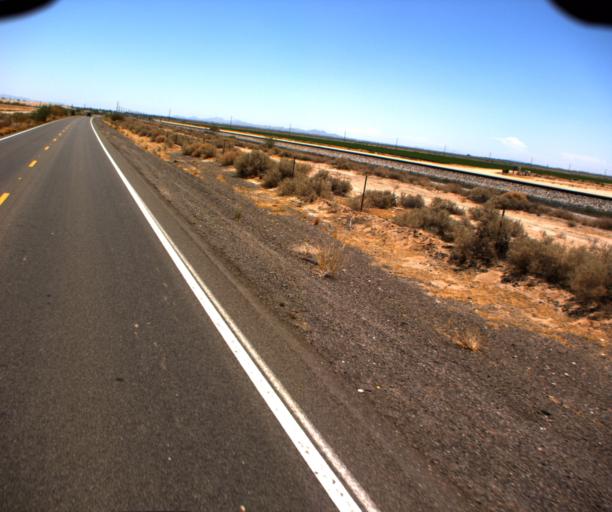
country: US
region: Arizona
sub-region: Pinal County
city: Maricopa
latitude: 33.0798
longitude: -112.1279
